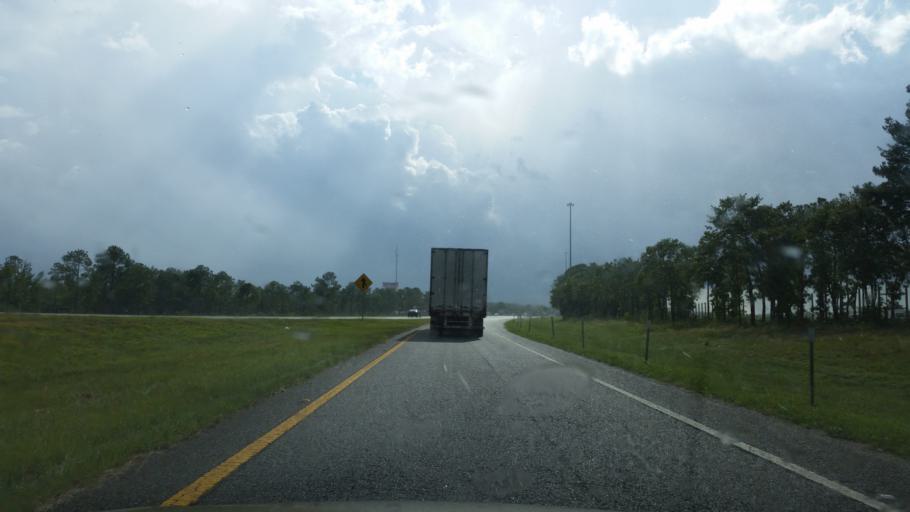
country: US
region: Florida
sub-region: Okaloosa County
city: Crestview
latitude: 30.7331
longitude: -86.3541
